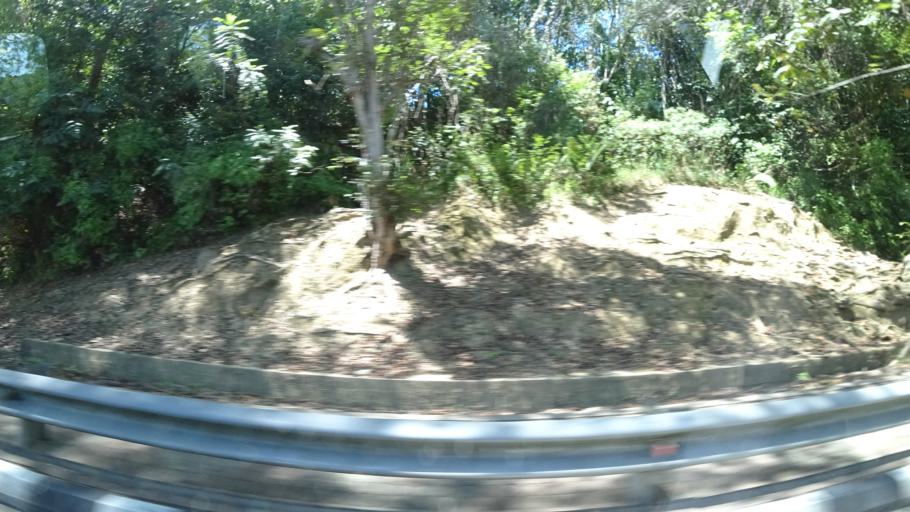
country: BN
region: Brunei and Muara
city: Bandar Seri Begawan
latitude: 4.8694
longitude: 114.9114
